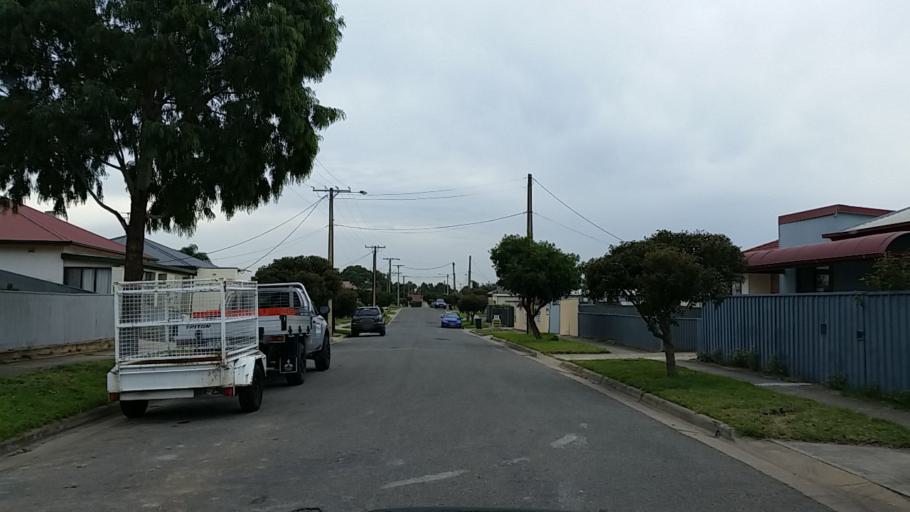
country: AU
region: South Australia
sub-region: Charles Sturt
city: Royal Park
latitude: -34.8769
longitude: 138.5063
